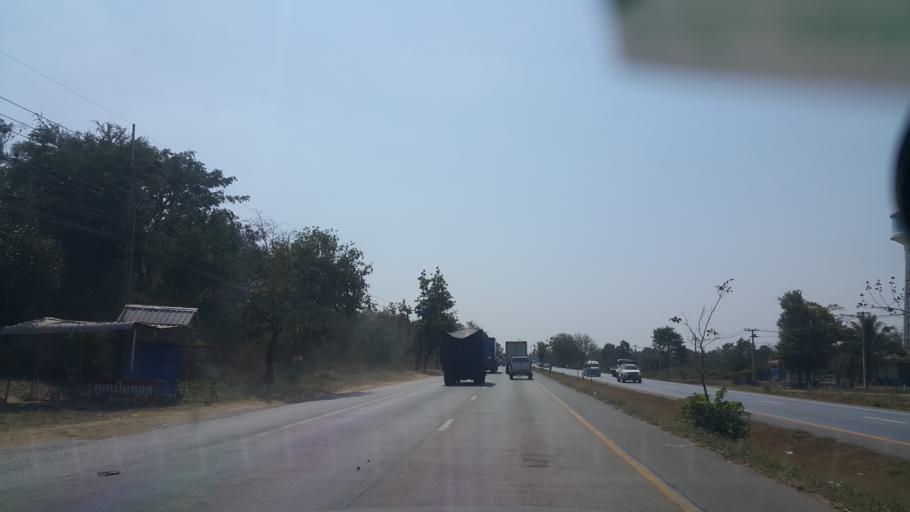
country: TH
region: Khon Kaen
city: Phon
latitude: 15.8419
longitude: 102.6133
